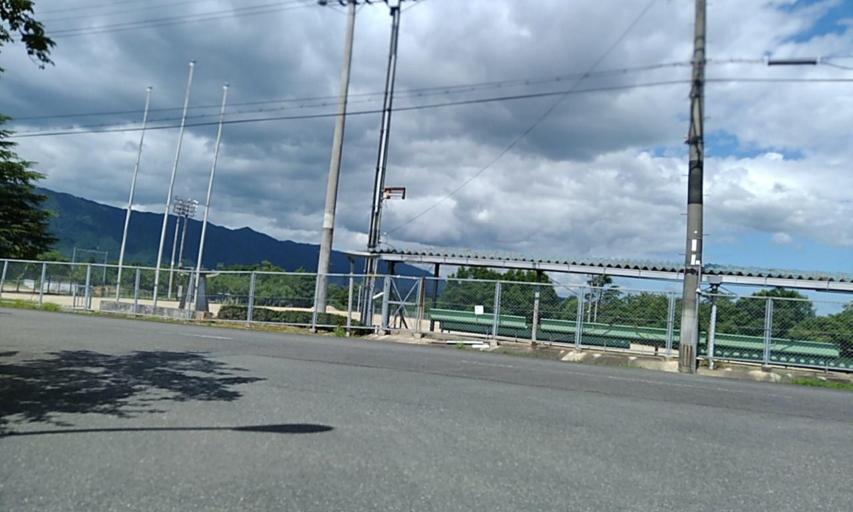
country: JP
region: Mie
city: Ueno-ebisumachi
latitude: 34.7525
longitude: 136.0147
